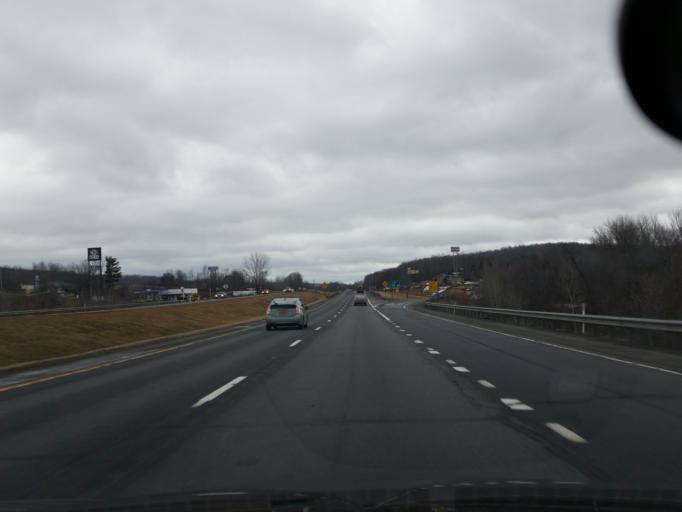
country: US
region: Pennsylvania
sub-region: Lackawanna County
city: Clarks Green
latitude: 41.5564
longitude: -75.6531
